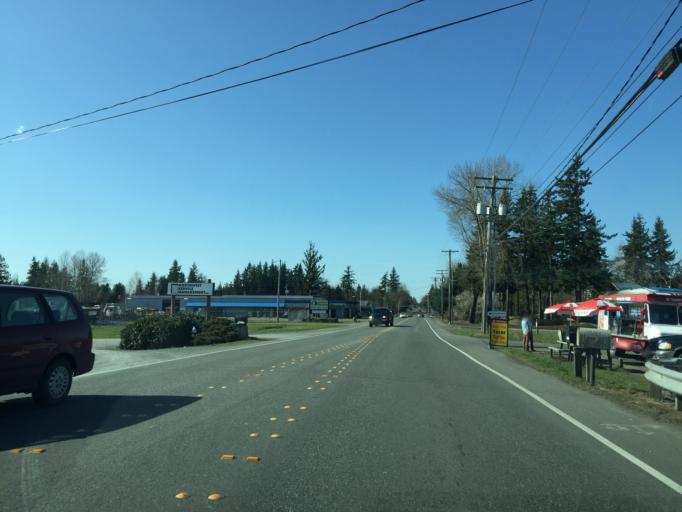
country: US
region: Washington
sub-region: Whatcom County
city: Bellingham
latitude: 48.7895
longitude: -122.4487
